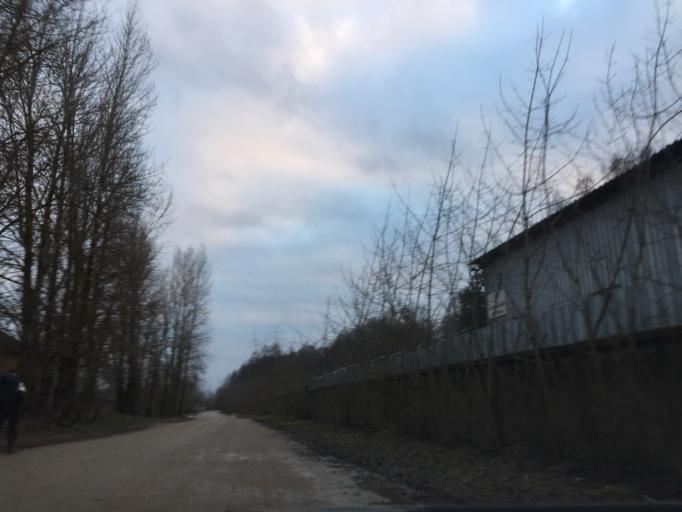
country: LV
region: Kekava
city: Kekava
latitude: 56.8966
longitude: 24.2019
